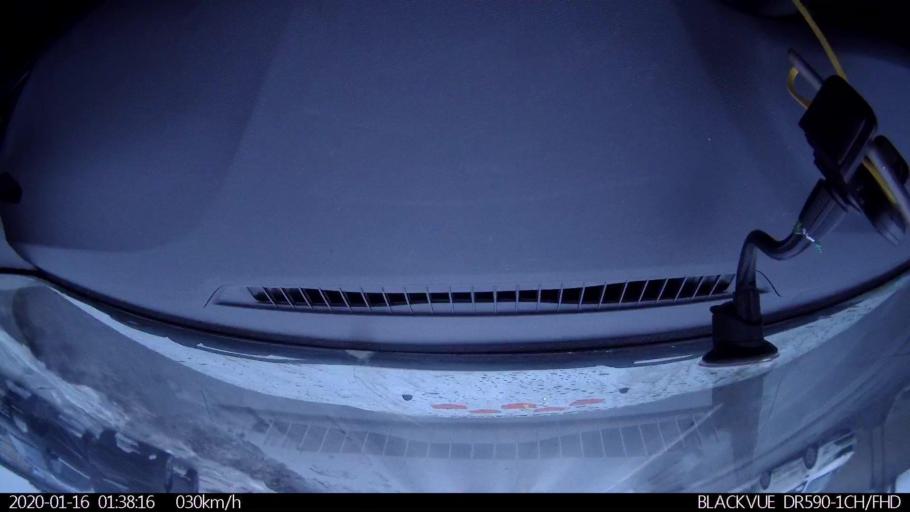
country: RU
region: Nizjnij Novgorod
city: Gorbatovka
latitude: 56.3379
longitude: 43.8030
